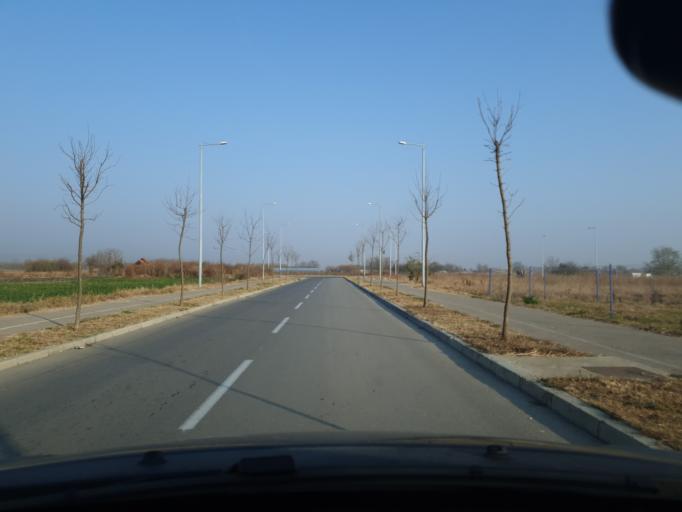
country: RS
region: Central Serbia
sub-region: Jablanicki Okrug
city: Leskovac
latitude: 43.0026
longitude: 21.9239
